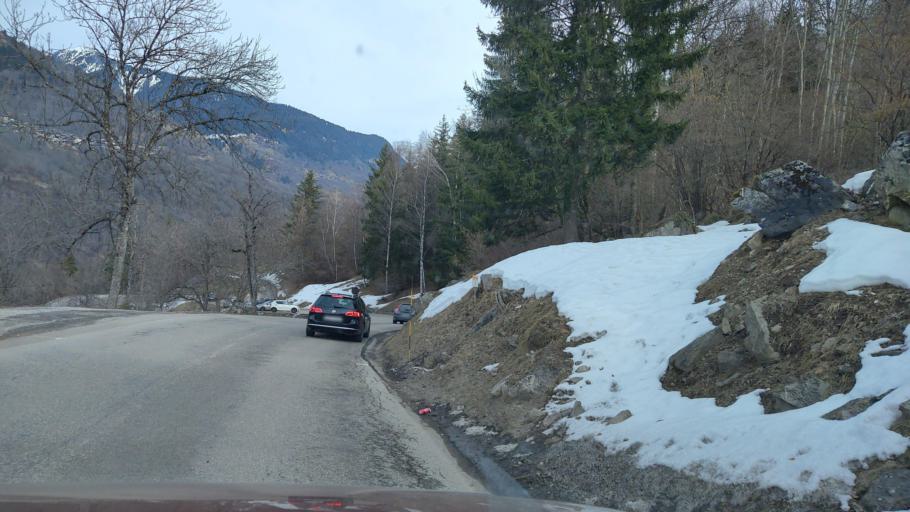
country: FR
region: Rhone-Alpes
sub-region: Departement de la Savoie
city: Saint-Bon-Tarentaise
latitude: 45.4415
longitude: 6.6167
